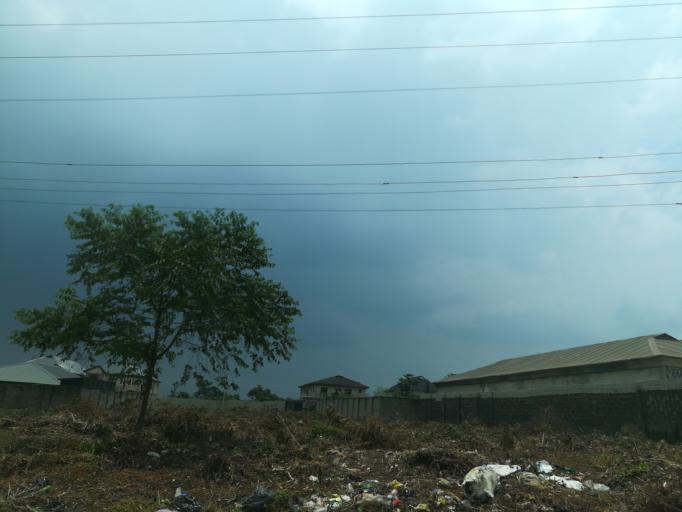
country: NG
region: Lagos
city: Ikorodu
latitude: 6.6128
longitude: 3.5781
